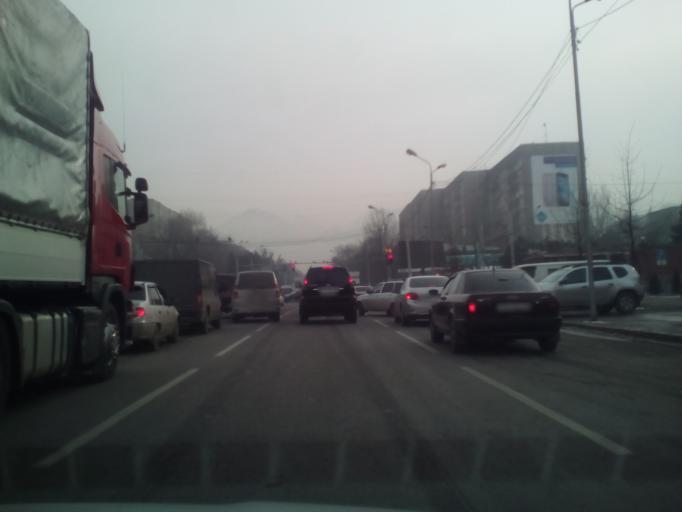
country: KZ
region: Almaty Qalasy
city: Almaty
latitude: 43.2401
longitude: 76.8290
